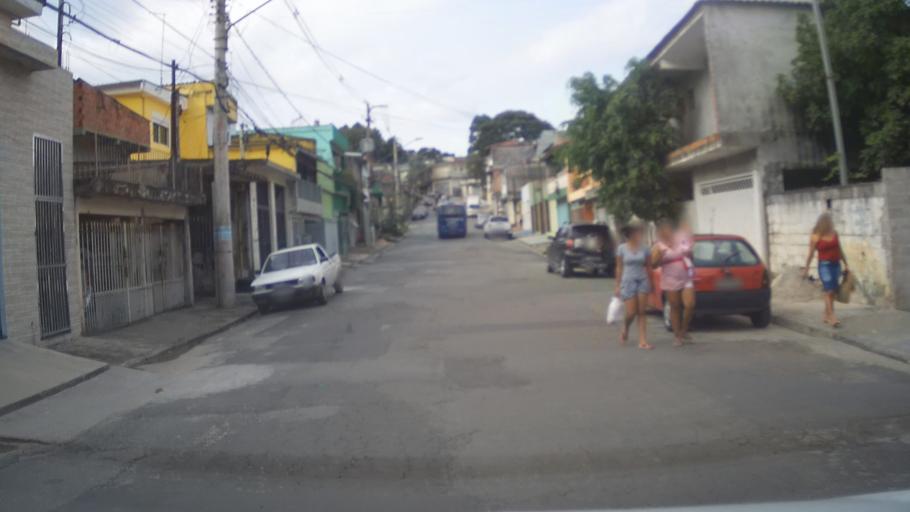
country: BR
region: Sao Paulo
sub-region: Guarulhos
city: Guarulhos
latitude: -23.4150
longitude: -46.5100
